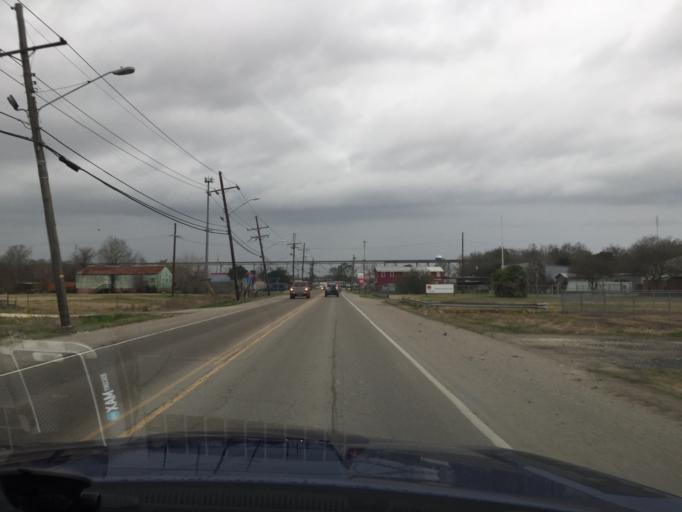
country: US
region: Louisiana
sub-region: Jefferson Parish
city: Bridge City
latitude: 29.9289
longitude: -90.1581
